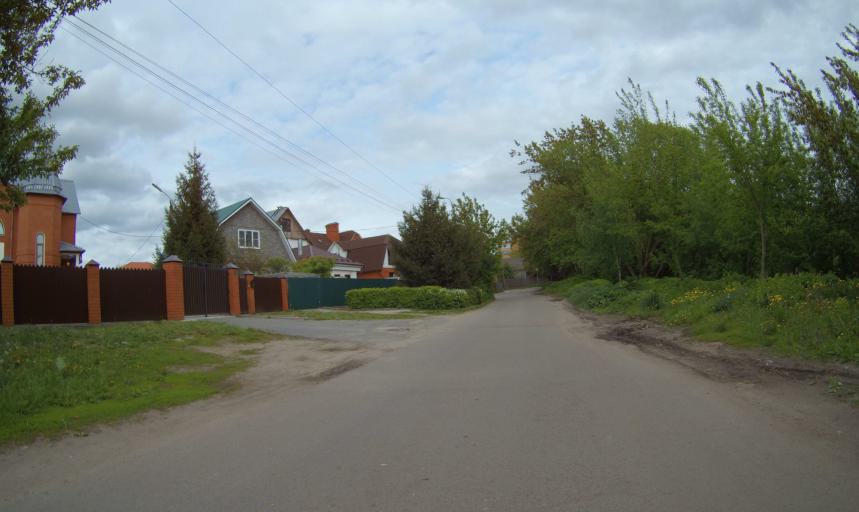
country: RU
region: Moskovskaya
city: Kolomna
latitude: 55.0962
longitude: 38.7542
